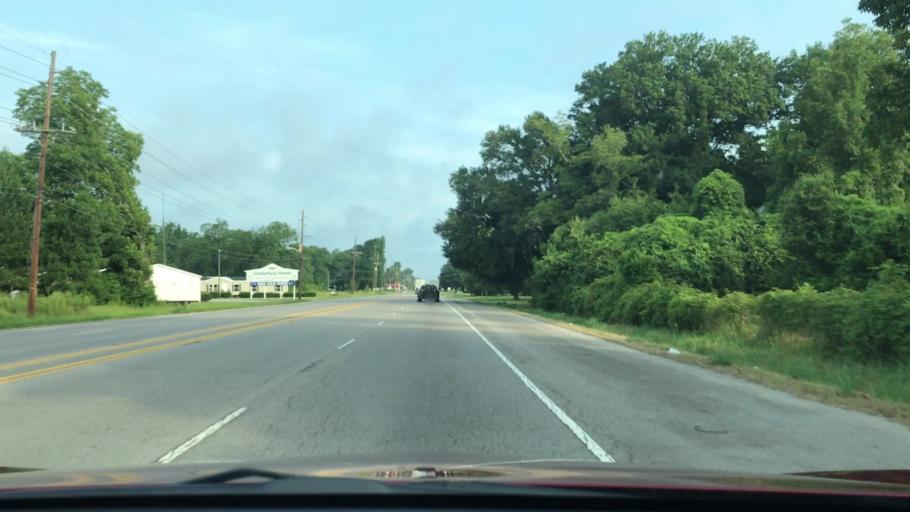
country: US
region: South Carolina
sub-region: Orangeburg County
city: Brookdale
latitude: 33.4743
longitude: -80.8112
